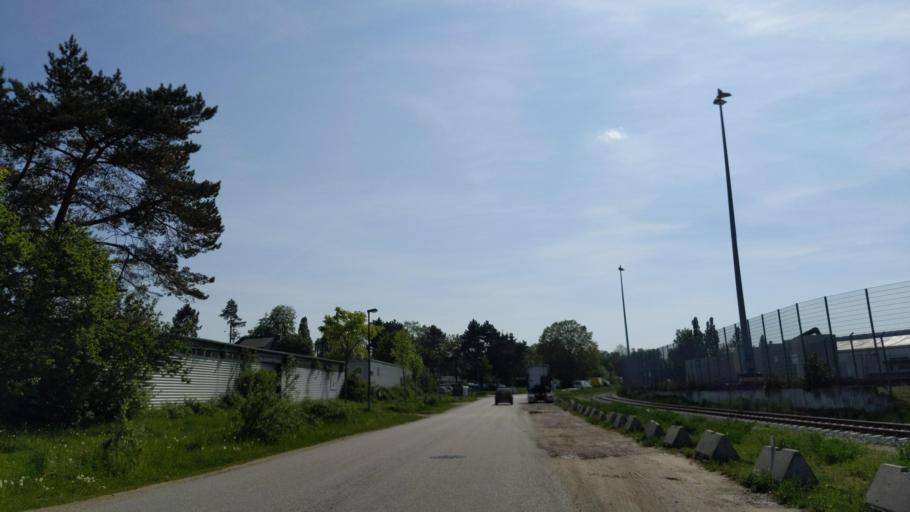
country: DE
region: Mecklenburg-Vorpommern
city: Selmsdorf
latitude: 53.8927
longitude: 10.7956
